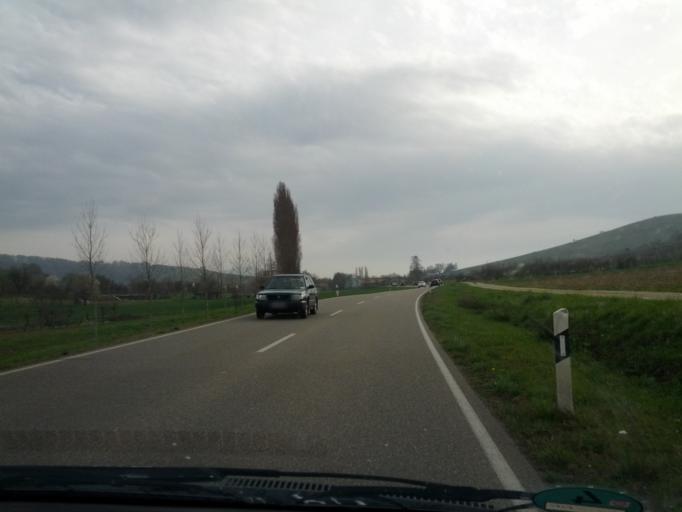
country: DE
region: Baden-Wuerttemberg
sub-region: Freiburg Region
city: Schallstadt
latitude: 47.9489
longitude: 7.7586
